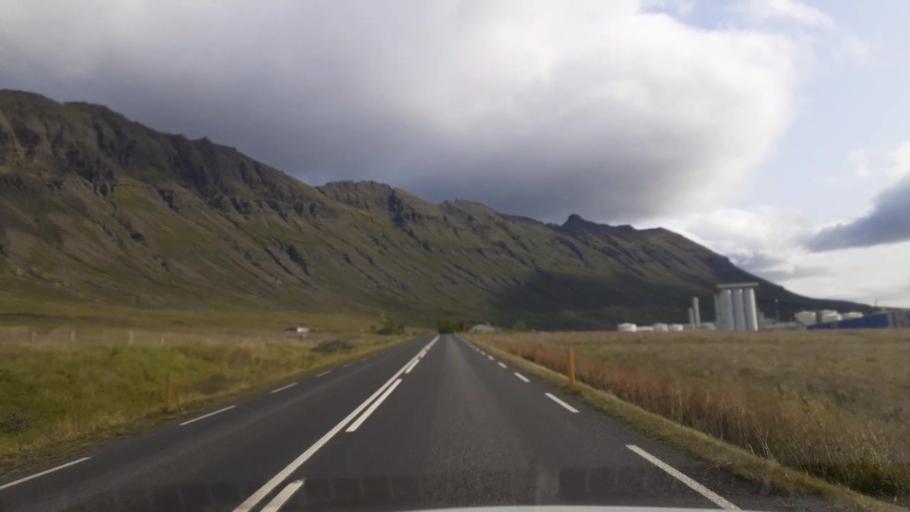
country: IS
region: East
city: Neskaupstadur
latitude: 65.1364
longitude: -13.7484
